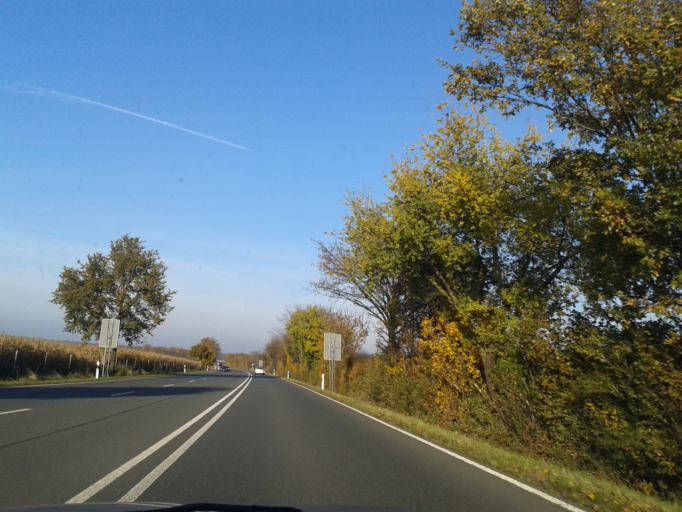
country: DE
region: North Rhine-Westphalia
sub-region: Regierungsbezirk Detmold
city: Salzkotten
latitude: 51.6384
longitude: 8.6513
